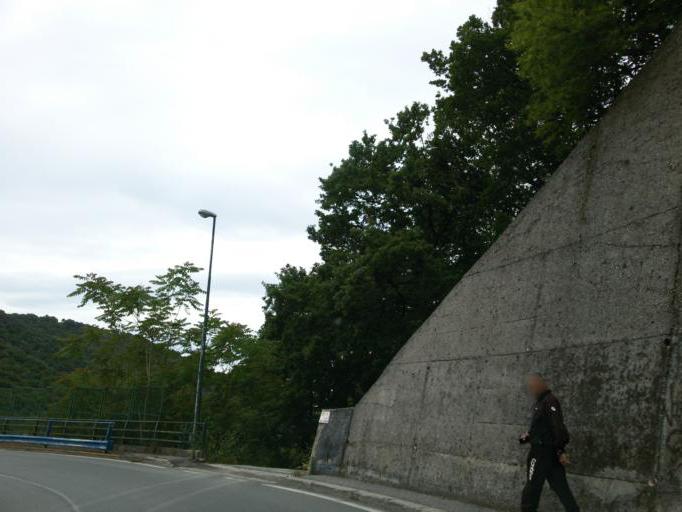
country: IT
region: Liguria
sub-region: Provincia di Genova
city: Piccarello
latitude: 44.4380
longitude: 8.9713
